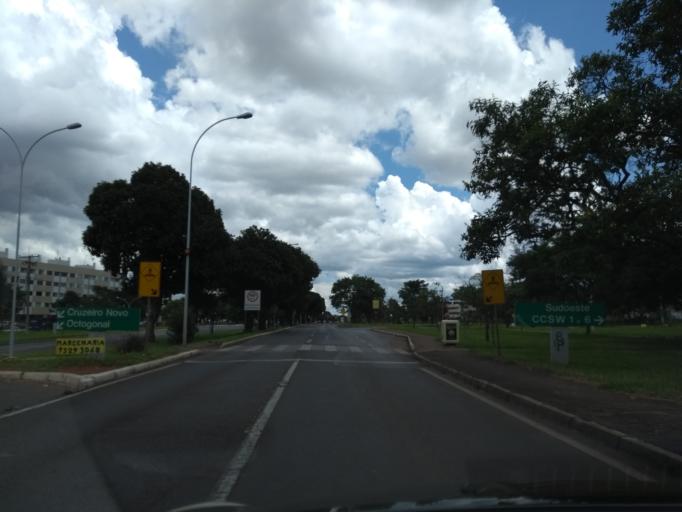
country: BR
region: Federal District
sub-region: Brasilia
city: Brasilia
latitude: -15.7974
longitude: -47.9334
